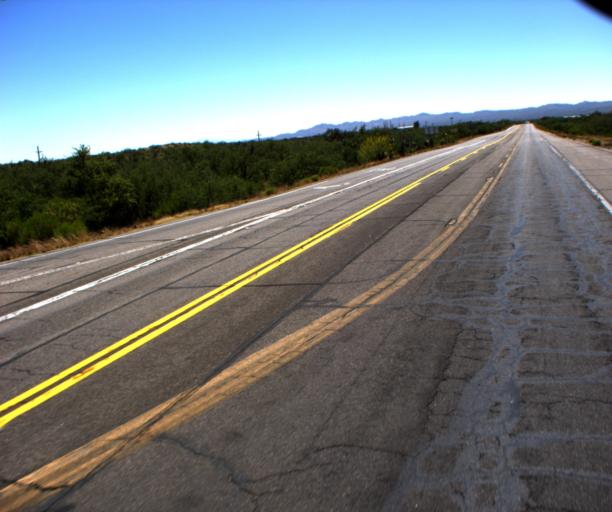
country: US
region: Arizona
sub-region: Pinal County
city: Oracle
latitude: 32.6209
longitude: -110.8020
